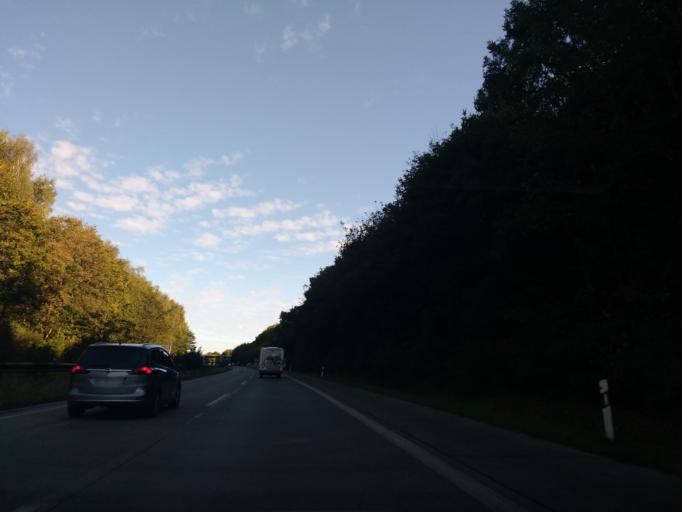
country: DE
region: Schleswig-Holstein
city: Ratekau
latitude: 53.9416
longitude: 10.7446
